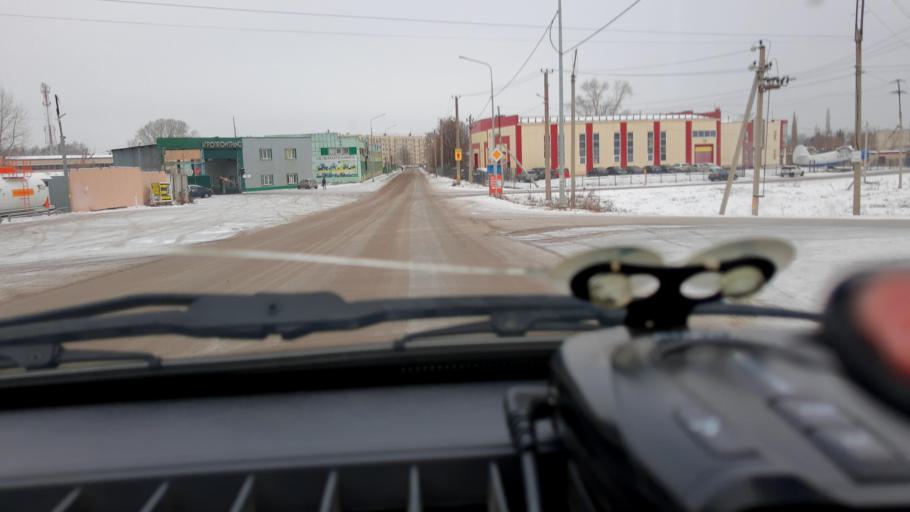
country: RU
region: Bashkortostan
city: Avdon
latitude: 54.6061
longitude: 55.8460
